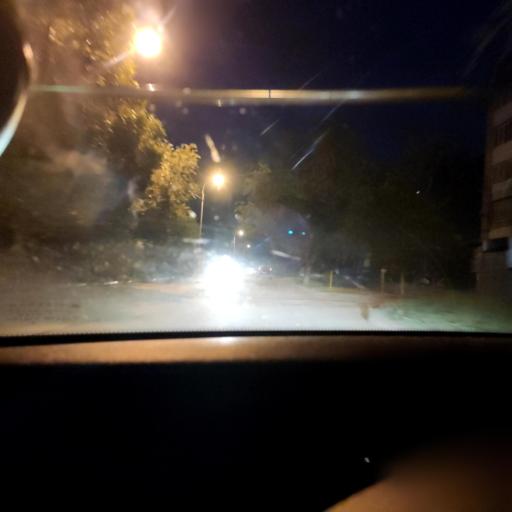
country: RU
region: Samara
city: Samara
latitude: 53.1235
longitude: 50.0959
